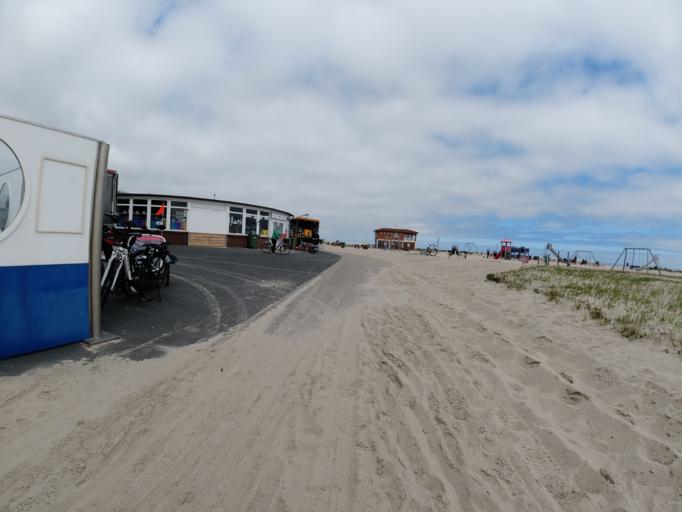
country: DE
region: Lower Saxony
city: Schillig
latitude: 53.7004
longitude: 8.0298
